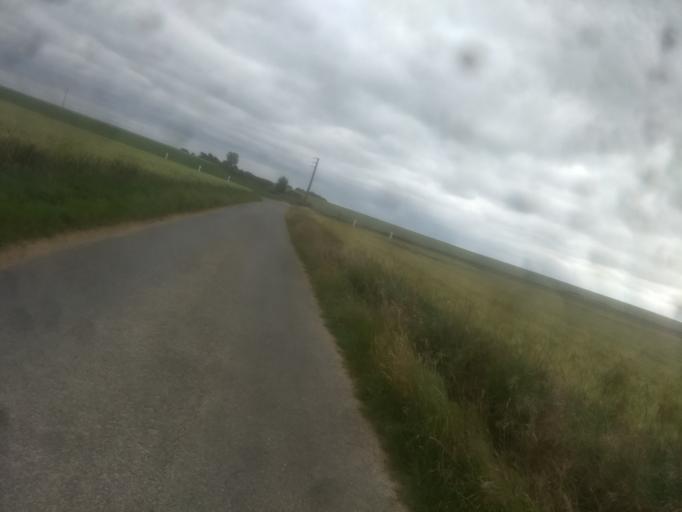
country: FR
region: Nord-Pas-de-Calais
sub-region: Departement du Pas-de-Calais
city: Mont-Saint-Eloi
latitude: 50.3521
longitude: 2.7134
